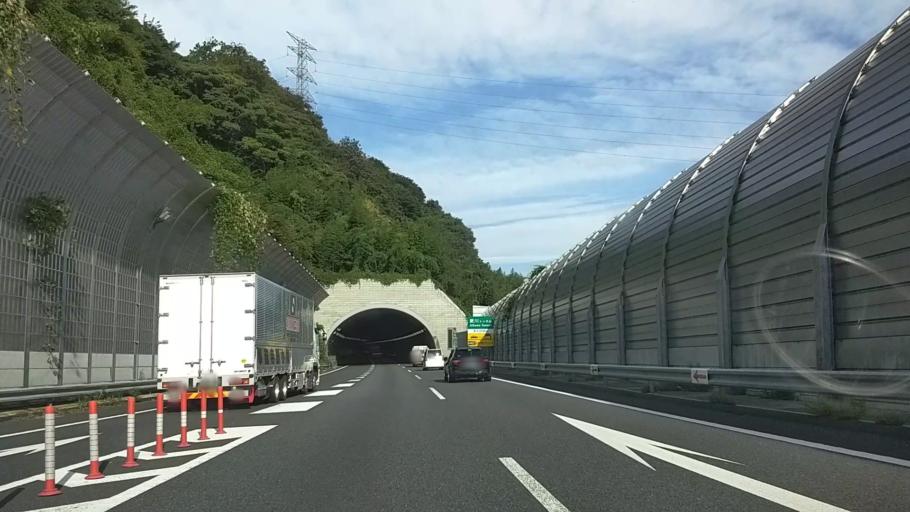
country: JP
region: Kanagawa
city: Zama
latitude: 35.5245
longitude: 139.3515
